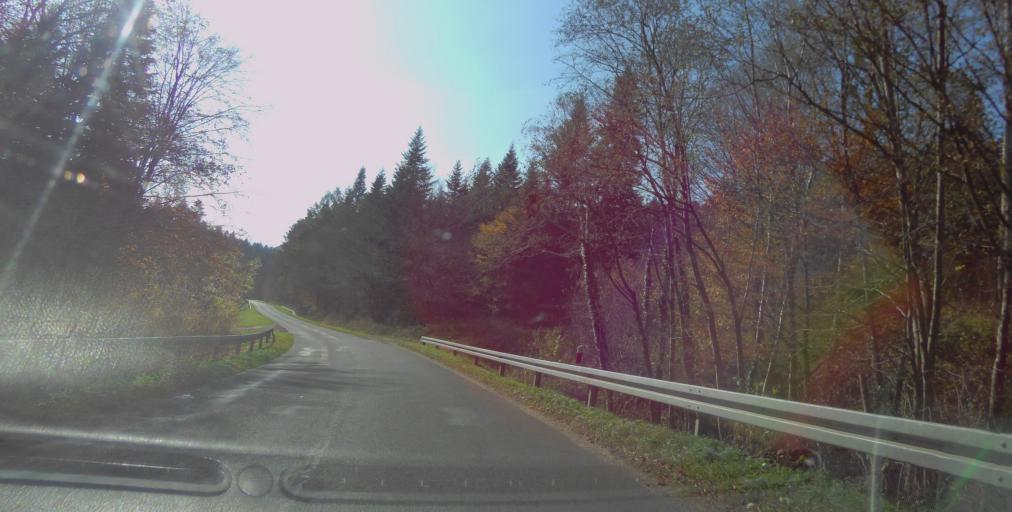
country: PL
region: Subcarpathian Voivodeship
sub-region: Powiat leski
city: Polanczyk
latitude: 49.3142
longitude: 22.4357
